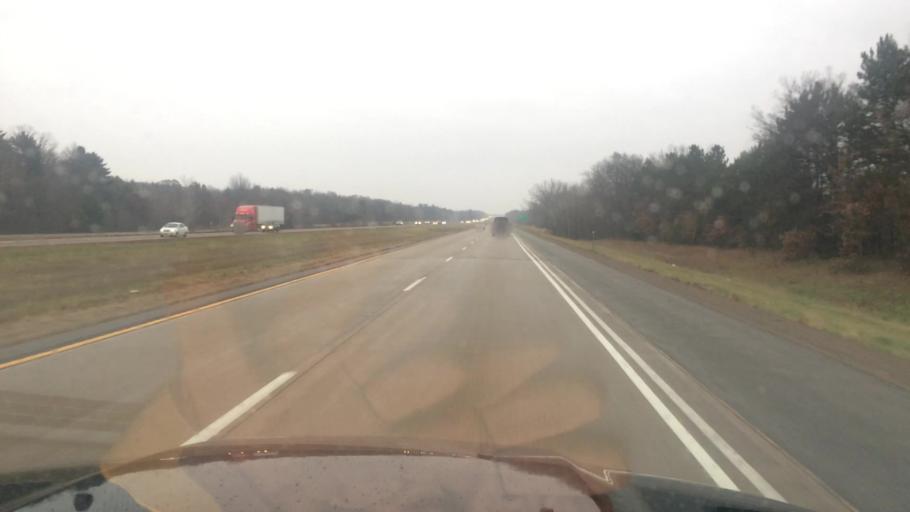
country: US
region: Wisconsin
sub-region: Portage County
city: Stevens Point
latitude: 44.6202
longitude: -89.6285
